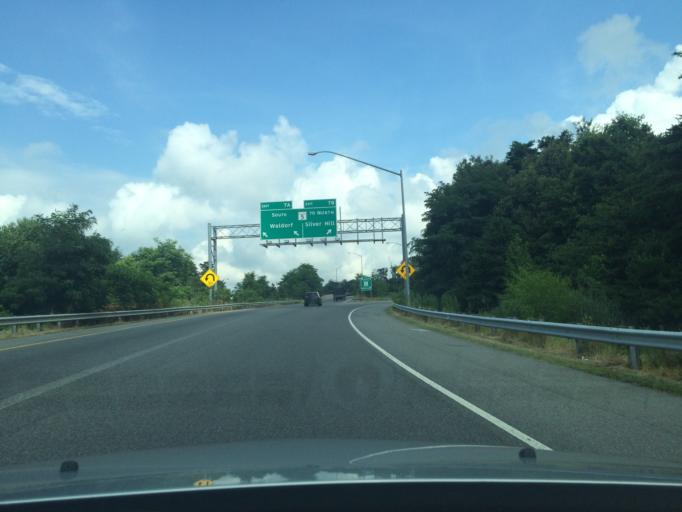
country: US
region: Maryland
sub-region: Prince George's County
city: Camp Springs
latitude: 38.8197
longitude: -76.9162
